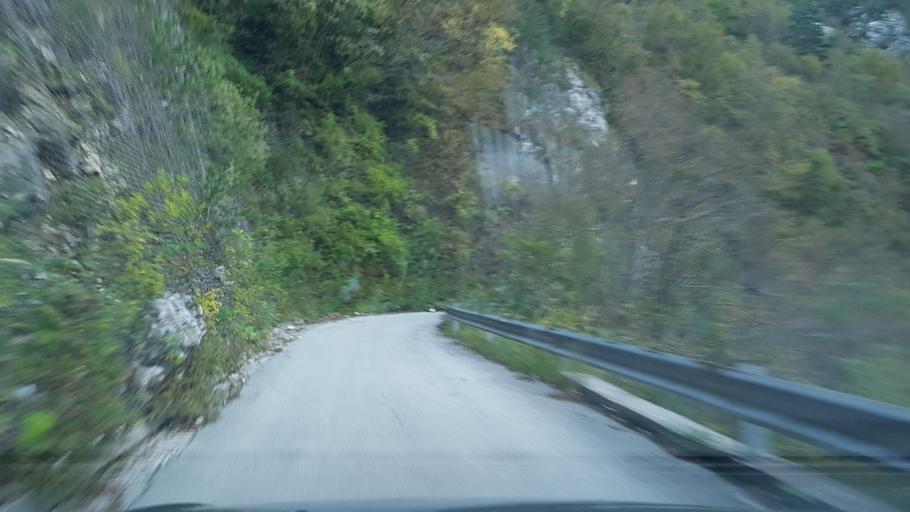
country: IT
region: Friuli Venezia Giulia
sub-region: Provincia di Udine
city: Venzone
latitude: 46.3348
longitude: 13.1806
